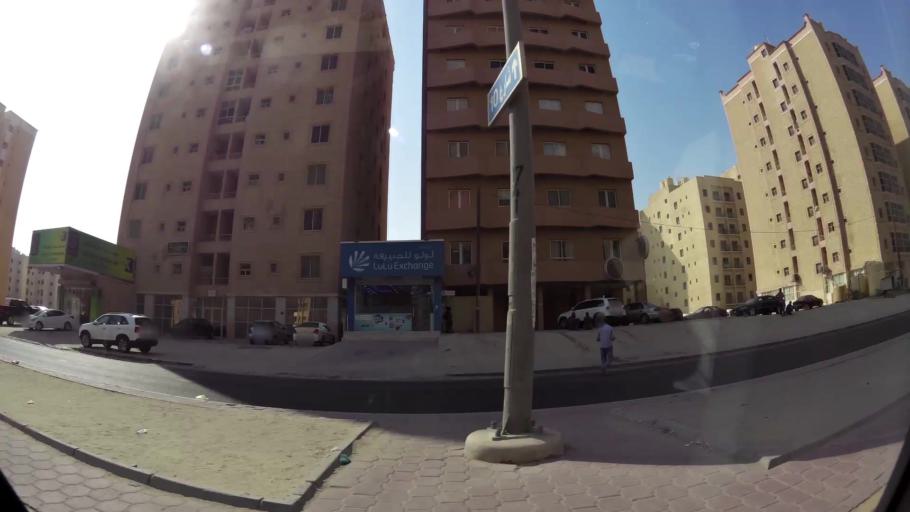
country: KW
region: Al Ahmadi
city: Al Mahbulah
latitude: 29.1560
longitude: 48.1159
